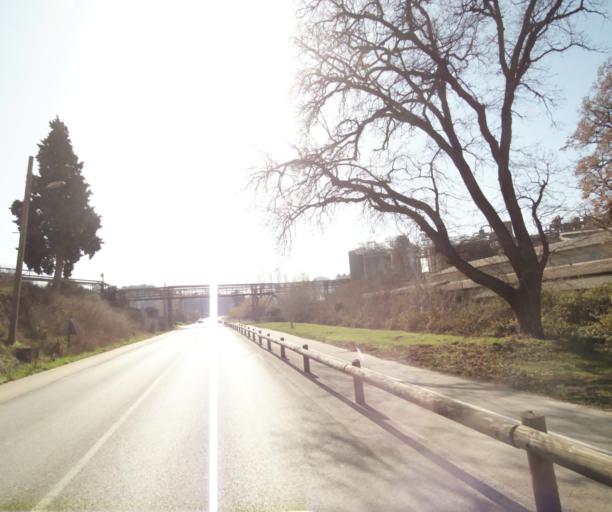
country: FR
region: Provence-Alpes-Cote d'Azur
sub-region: Departement des Bouches-du-Rhone
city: Gardanne
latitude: 43.4527
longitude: 5.4643
